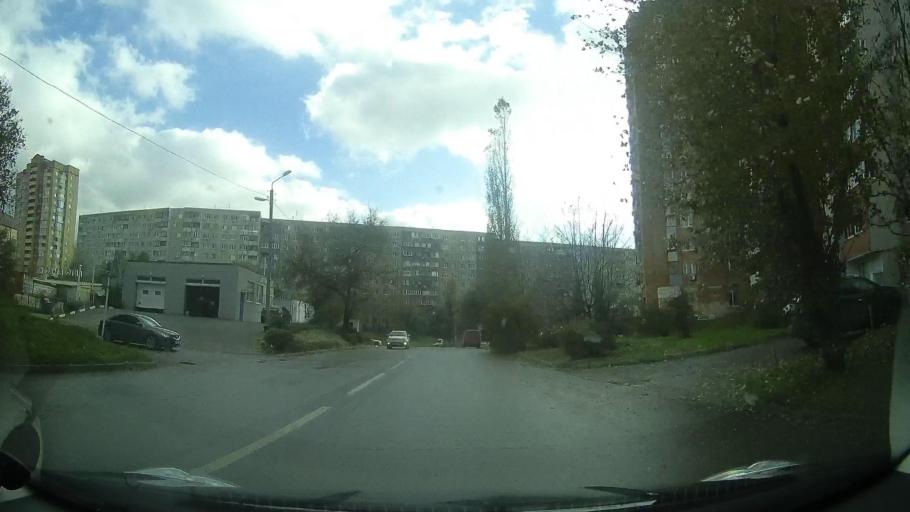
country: RU
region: Rostov
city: Severnyy
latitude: 47.2938
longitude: 39.6960
